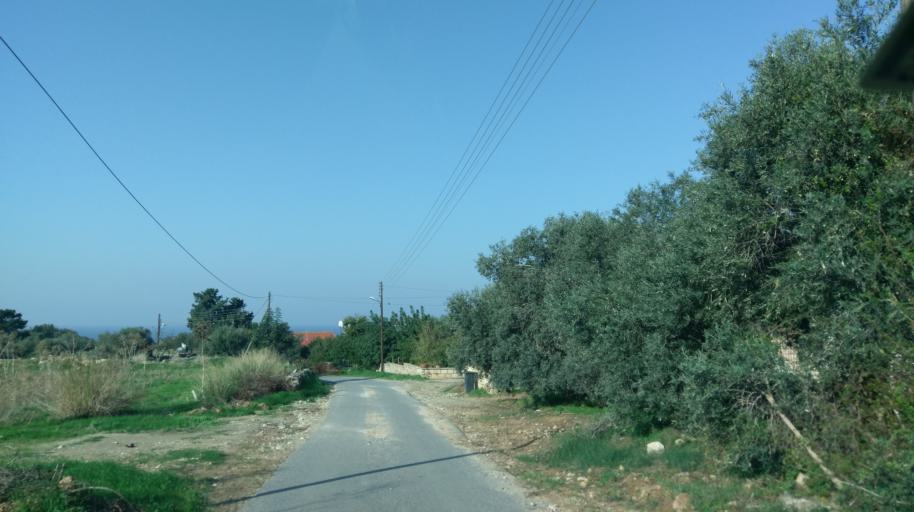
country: CY
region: Ammochostos
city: Leonarisso
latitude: 35.5385
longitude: 34.1886
